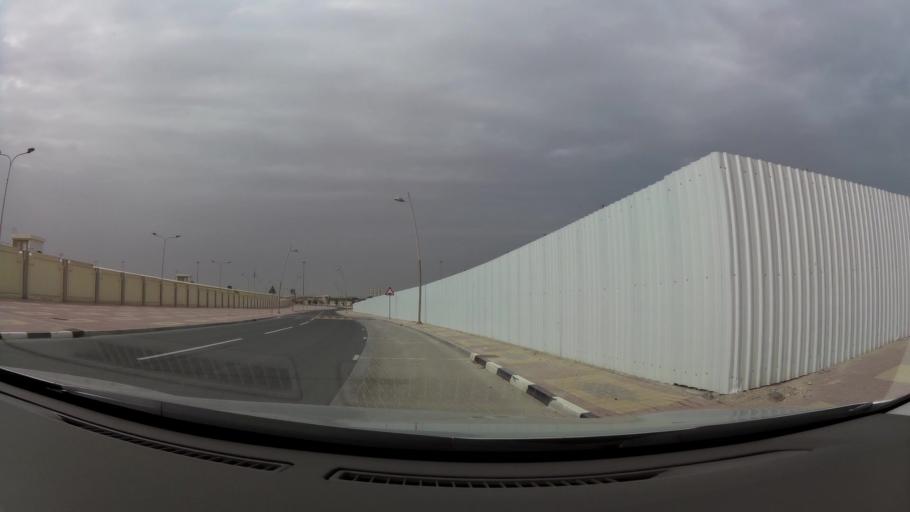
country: QA
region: Baladiyat ad Dawhah
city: Doha
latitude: 25.3465
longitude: 51.4855
